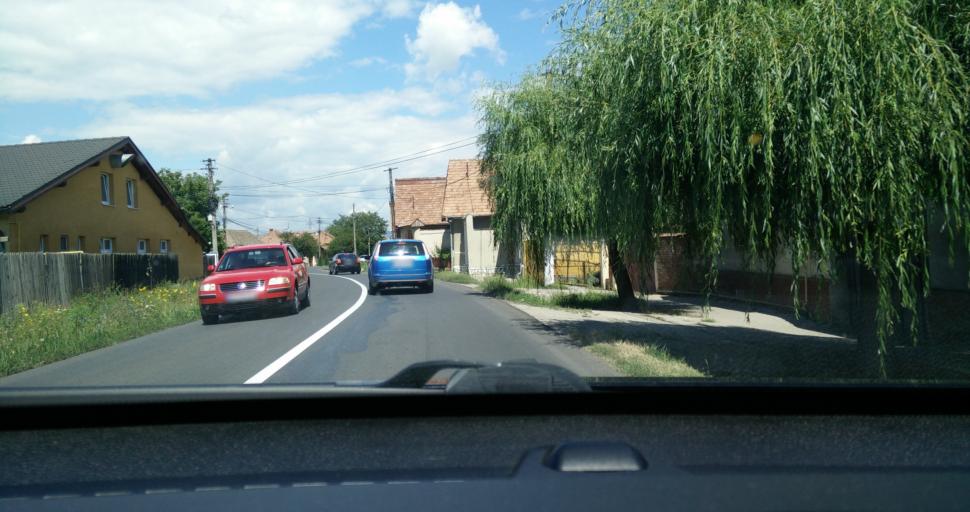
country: RO
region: Alba
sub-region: Municipiul Sebes
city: Petresti
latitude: 45.9277
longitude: 23.5608
